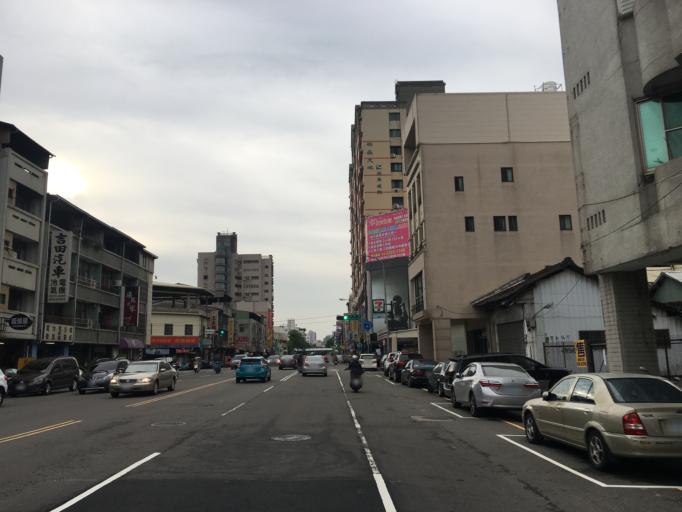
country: TW
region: Taiwan
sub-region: Taichung City
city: Taichung
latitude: 24.1370
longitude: 120.6715
